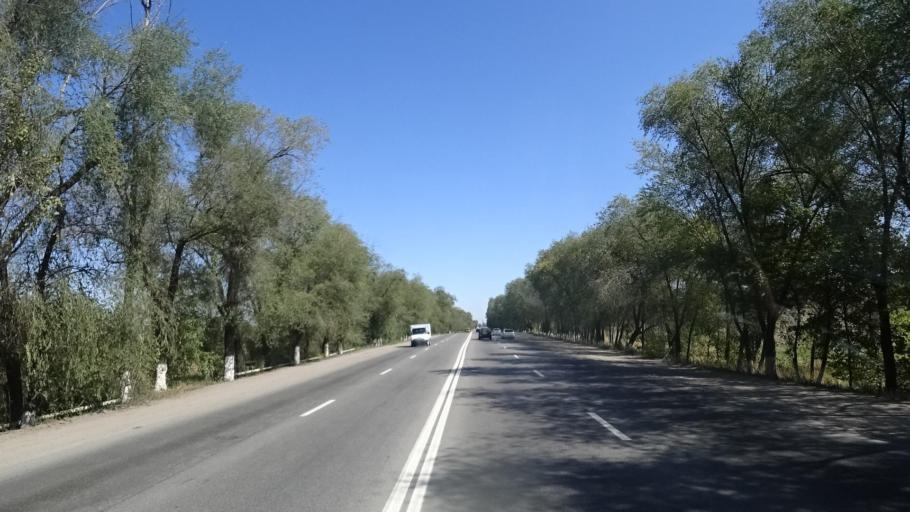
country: KZ
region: Almaty Oblysy
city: Energeticheskiy
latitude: 43.3756
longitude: 77.1004
